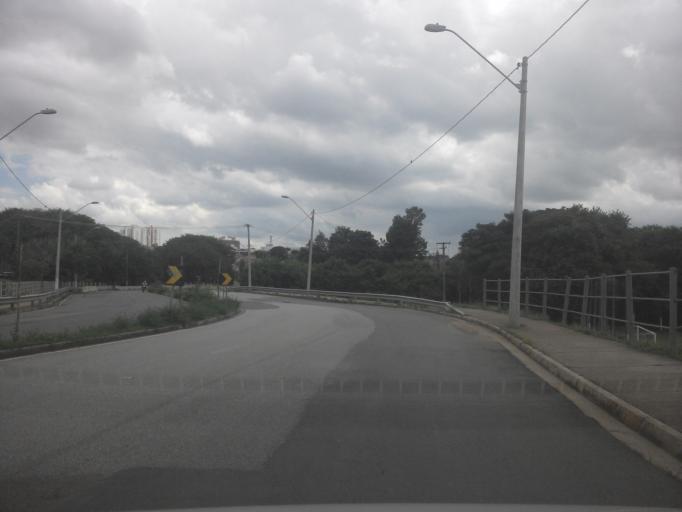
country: BR
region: Sao Paulo
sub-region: Campinas
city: Campinas
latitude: -22.8743
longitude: -47.0356
